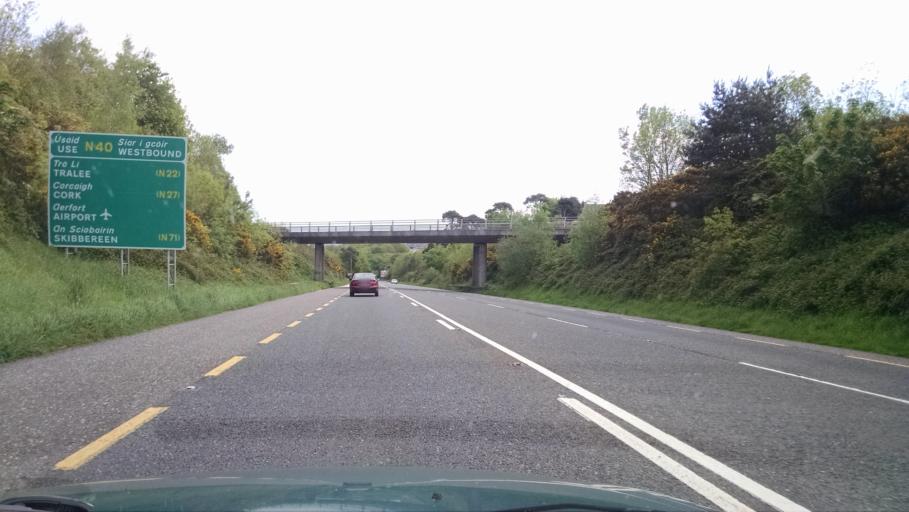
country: IE
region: Munster
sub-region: County Cork
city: Carrigaline
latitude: 51.8657
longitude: -8.4162
